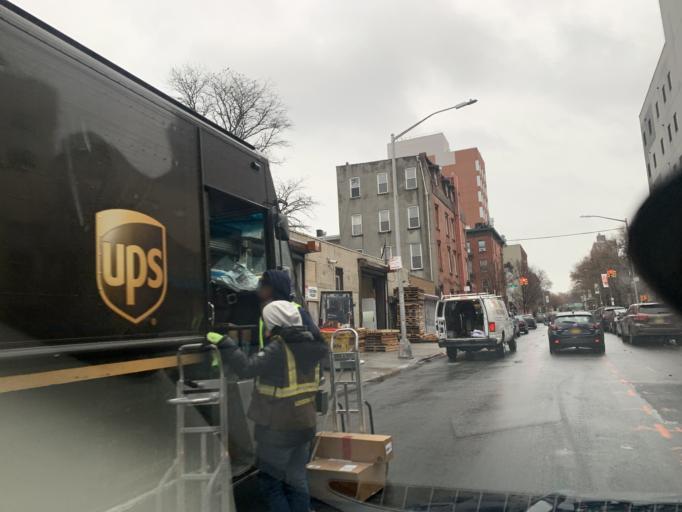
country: US
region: New York
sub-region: Kings County
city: Brooklyn
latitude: 40.6946
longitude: -73.9624
